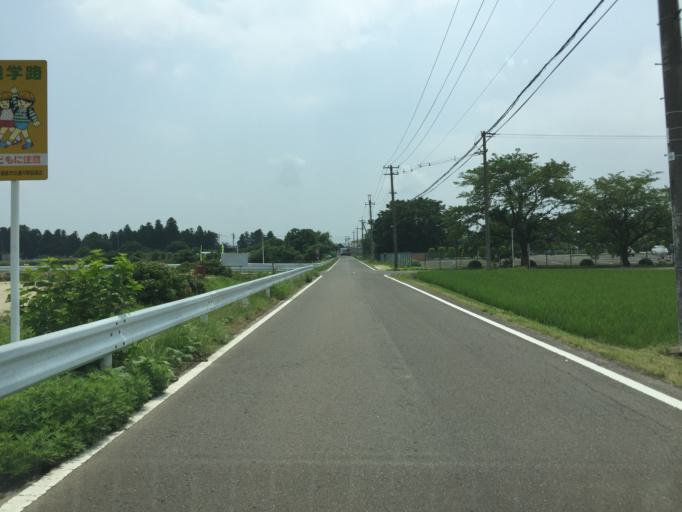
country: JP
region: Fukushima
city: Fukushima-shi
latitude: 37.7632
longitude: 140.3740
